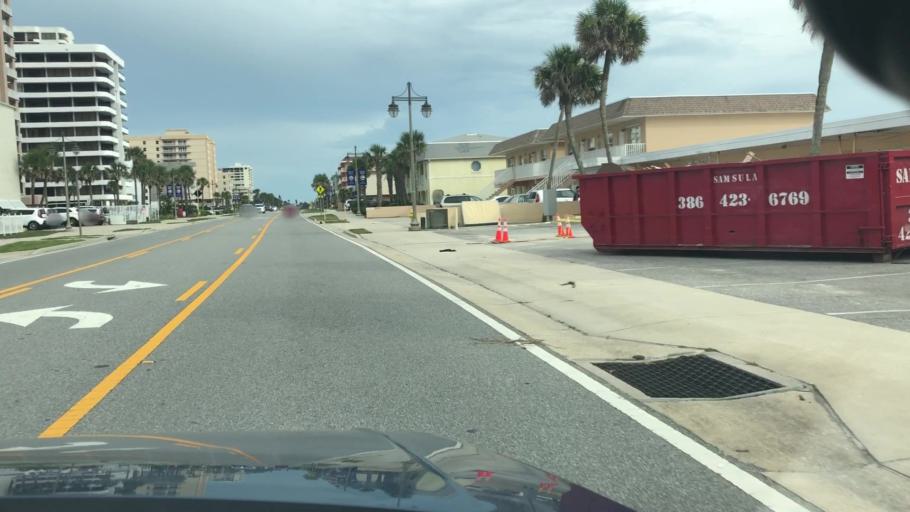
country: US
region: Florida
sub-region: Volusia County
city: Port Orange
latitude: 29.1448
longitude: -80.9658
